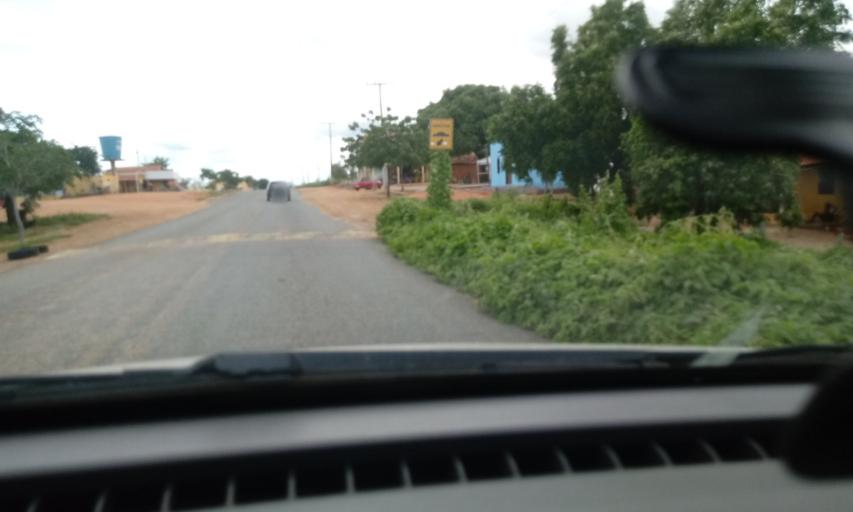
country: BR
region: Bahia
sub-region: Guanambi
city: Guanambi
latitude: -14.1149
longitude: -42.8606
